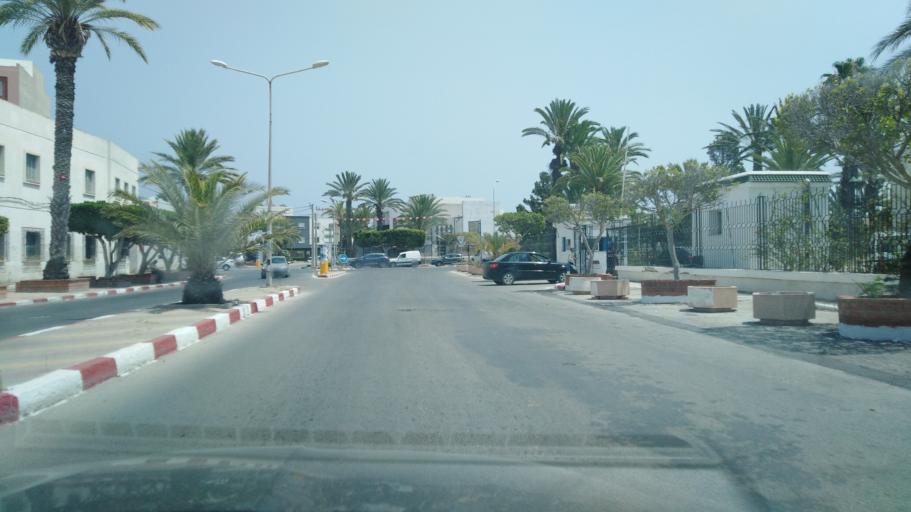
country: TN
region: Al Mahdiyah
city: Mahdia
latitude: 35.5064
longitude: 11.0551
